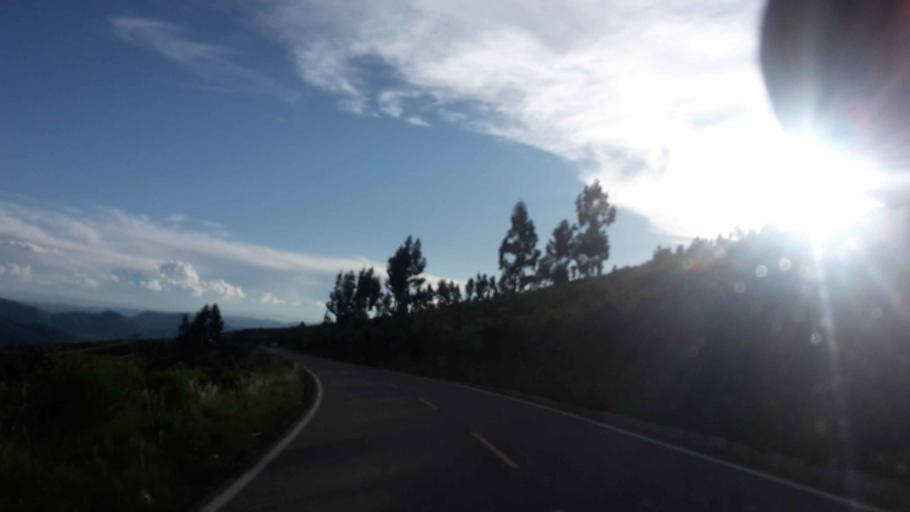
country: BO
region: Cochabamba
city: Arani
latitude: -17.5622
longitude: -65.7164
